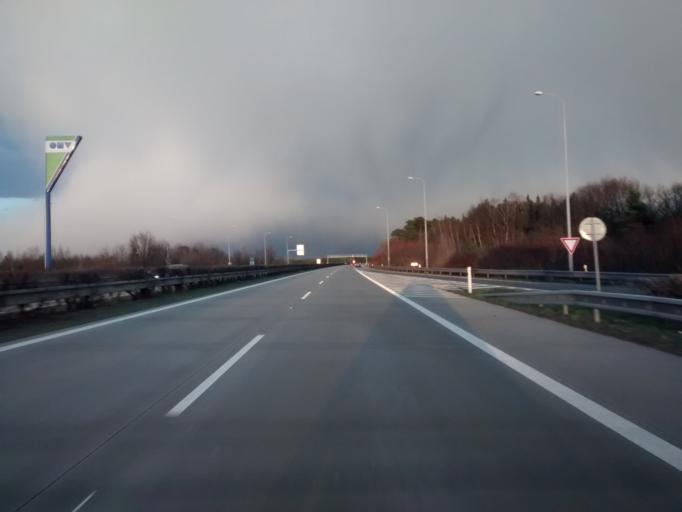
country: CZ
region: Central Bohemia
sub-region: Okres Nymburk
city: Podebrady
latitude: 50.1211
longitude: 15.0844
